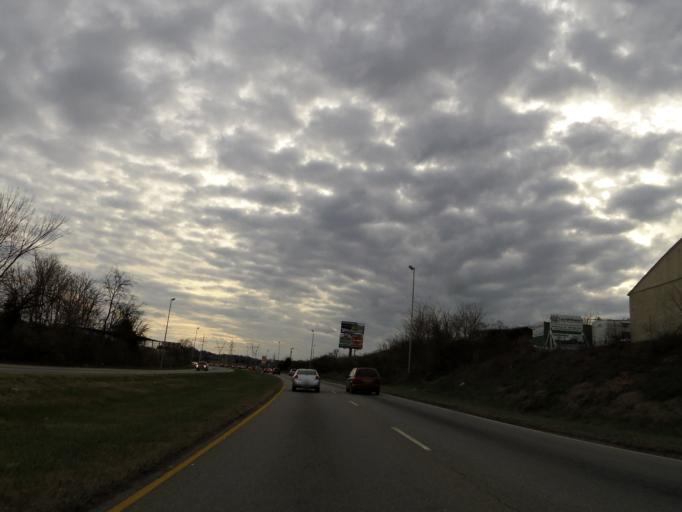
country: US
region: Tennessee
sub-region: Blount County
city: Maryville
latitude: 35.7565
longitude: -83.9930
